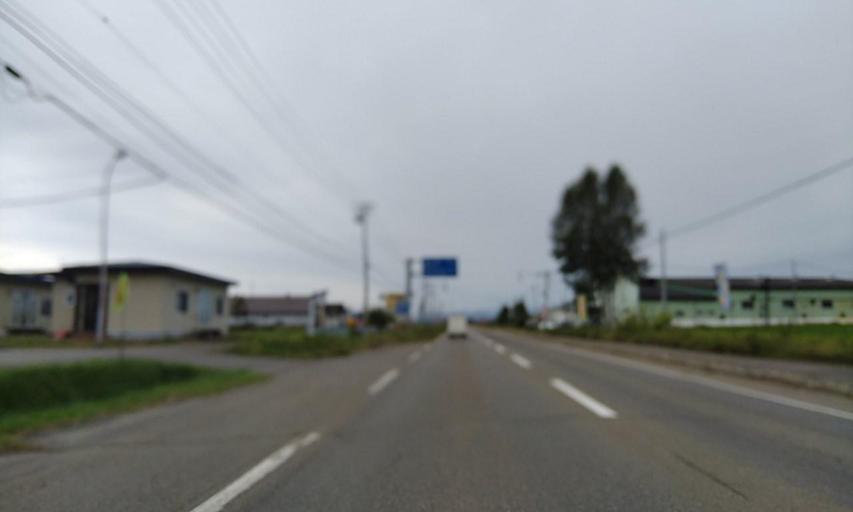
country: JP
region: Hokkaido
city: Obihiro
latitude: 42.7891
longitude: 143.1611
